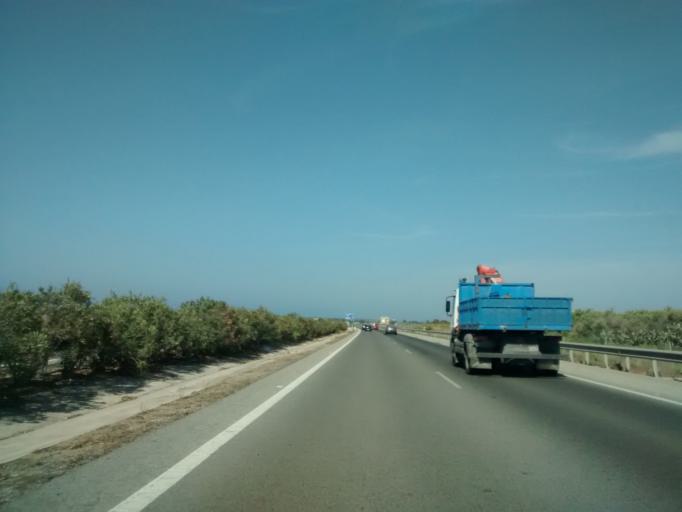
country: ES
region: Andalusia
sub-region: Provincia de Cadiz
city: Conil de la Frontera
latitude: 36.3549
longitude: -6.0814
